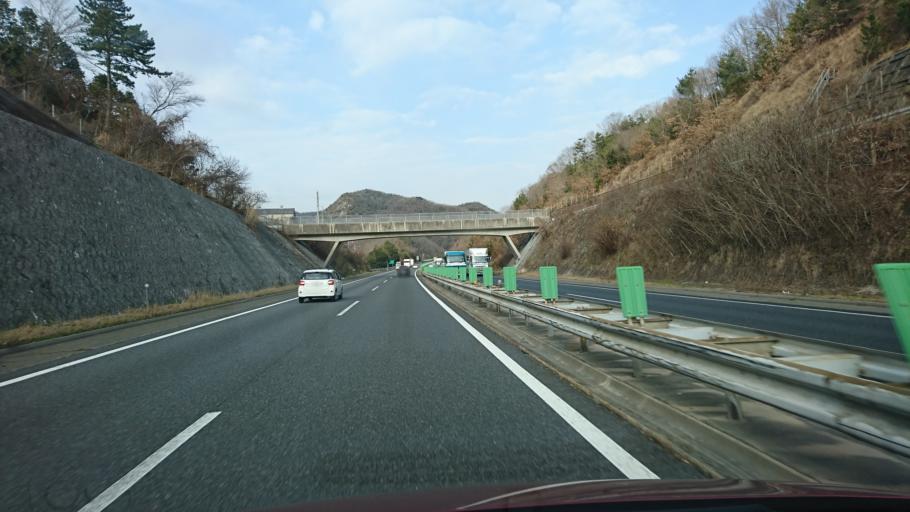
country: JP
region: Hyogo
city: Kariya
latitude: 34.7816
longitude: 134.2238
